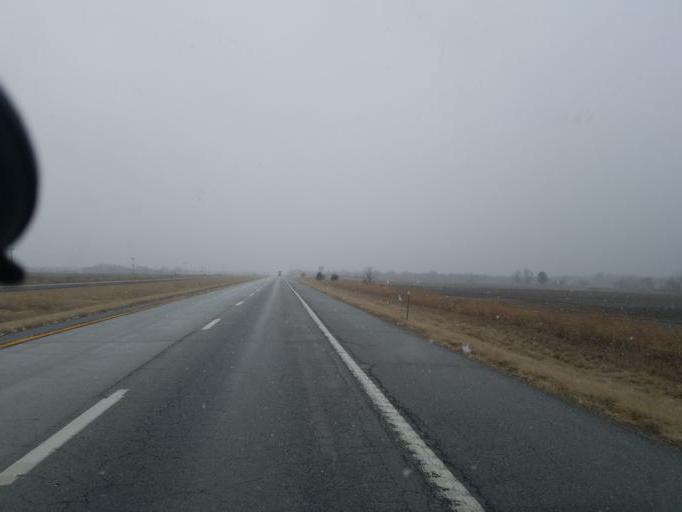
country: US
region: Missouri
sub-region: Macon County
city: La Plata
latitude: 39.9384
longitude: -92.4772
